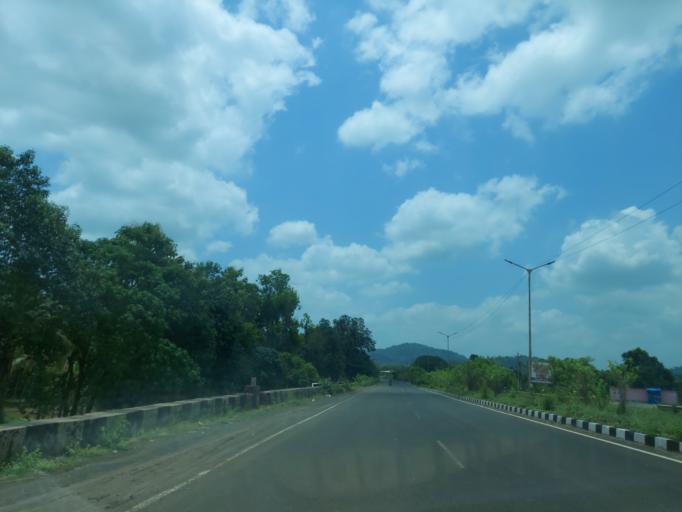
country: IN
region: Maharashtra
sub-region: Sindhudurg
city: Savantvadi
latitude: 15.8204
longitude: 73.8611
